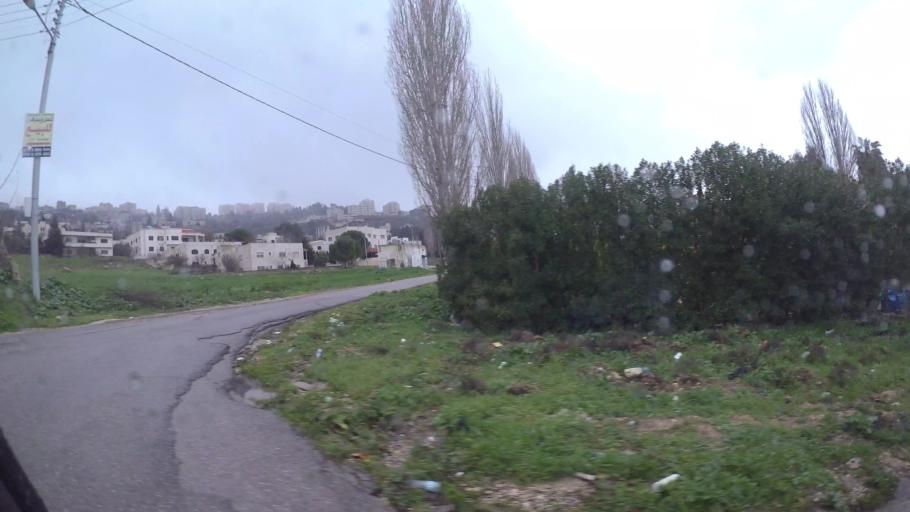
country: JO
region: Amman
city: Al Jubayhah
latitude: 32.0364
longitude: 35.8343
